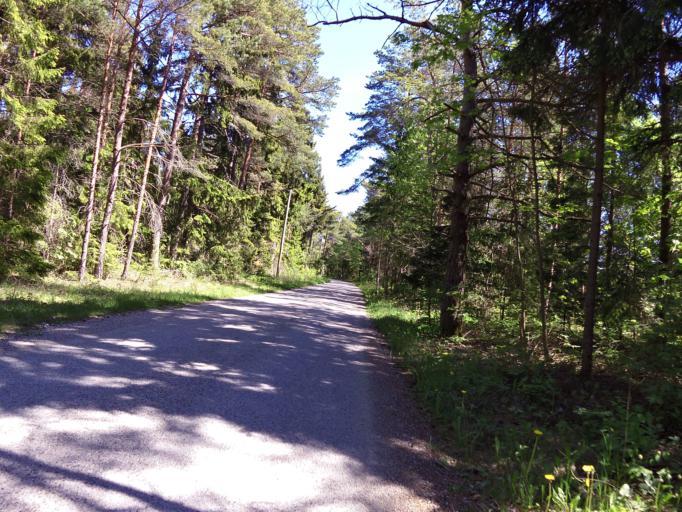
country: EE
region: Harju
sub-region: Paldiski linn
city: Paldiski
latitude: 59.2683
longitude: 23.7623
